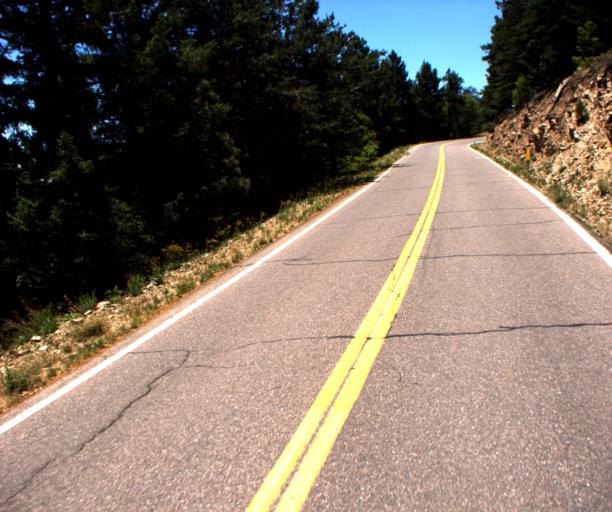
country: US
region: Arizona
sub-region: Graham County
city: Swift Trail Junction
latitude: 32.6451
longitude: -109.8555
